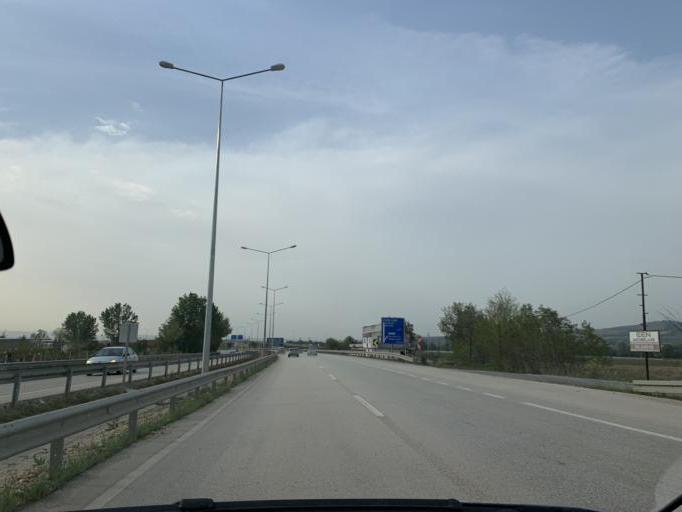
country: TR
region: Bursa
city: Kursunlu
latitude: 40.0549
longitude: 29.5876
